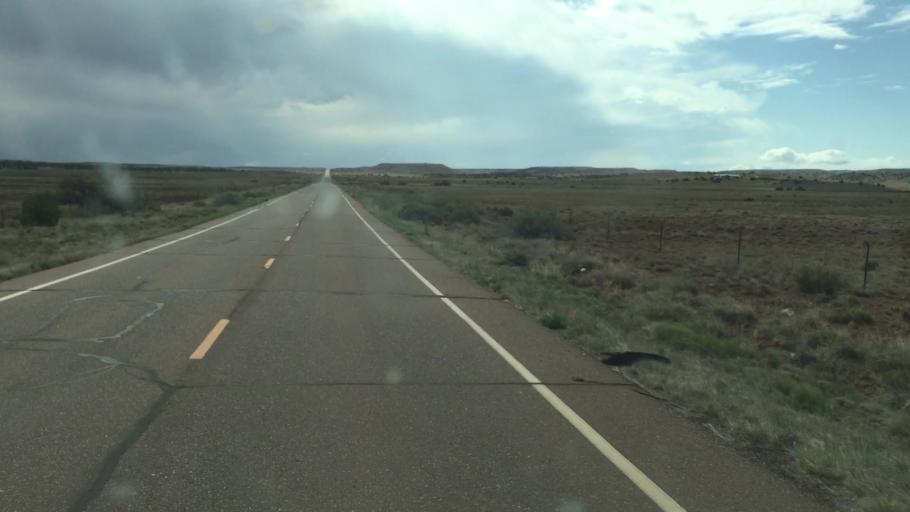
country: US
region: Arizona
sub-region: Apache County
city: Saint Johns
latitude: 34.5093
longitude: -109.6811
